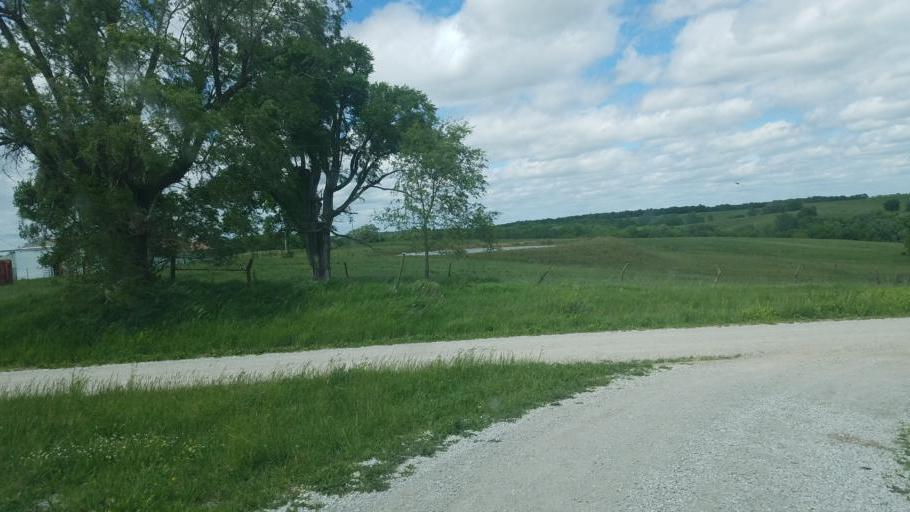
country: US
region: Iowa
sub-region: Decatur County
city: Lamoni
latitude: 40.5585
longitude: -94.0230
